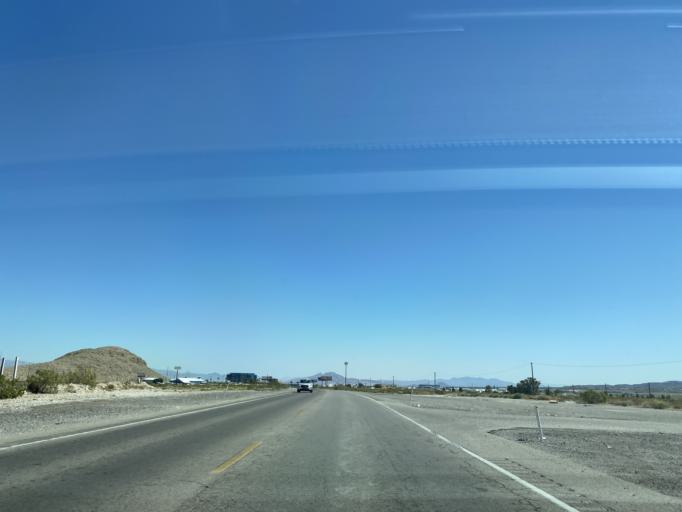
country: US
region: Nevada
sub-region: Clark County
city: Enterprise
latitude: 35.9432
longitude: -115.1816
